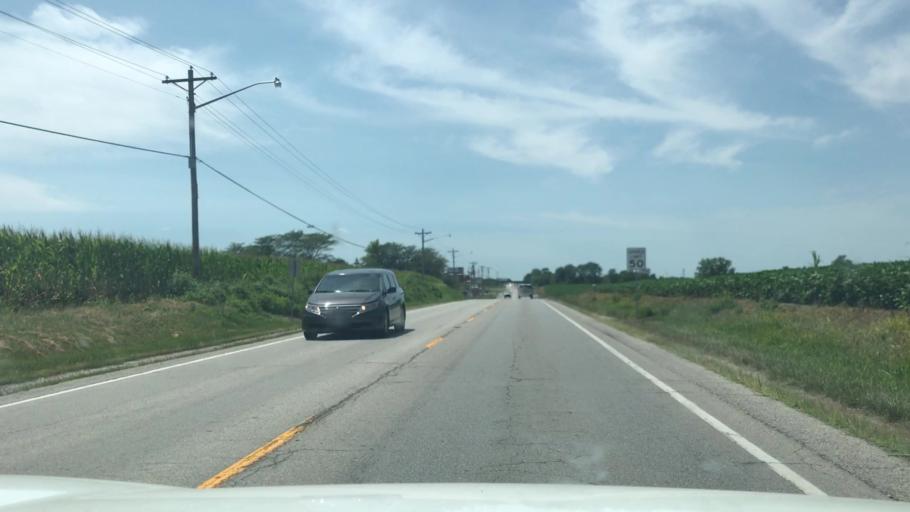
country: US
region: Illinois
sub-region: Clinton County
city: New Baden
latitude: 38.5353
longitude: -89.7160
